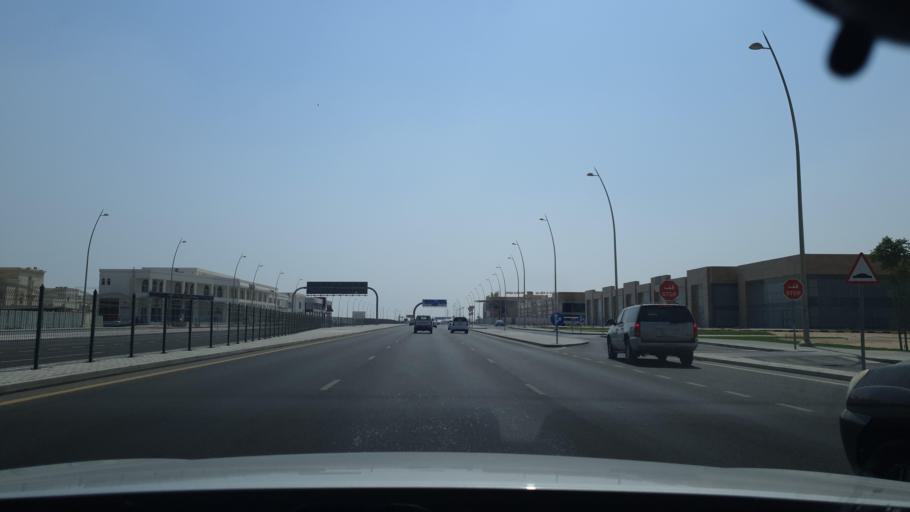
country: QA
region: Al Khawr
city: Al Khawr
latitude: 25.6700
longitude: 51.5009
